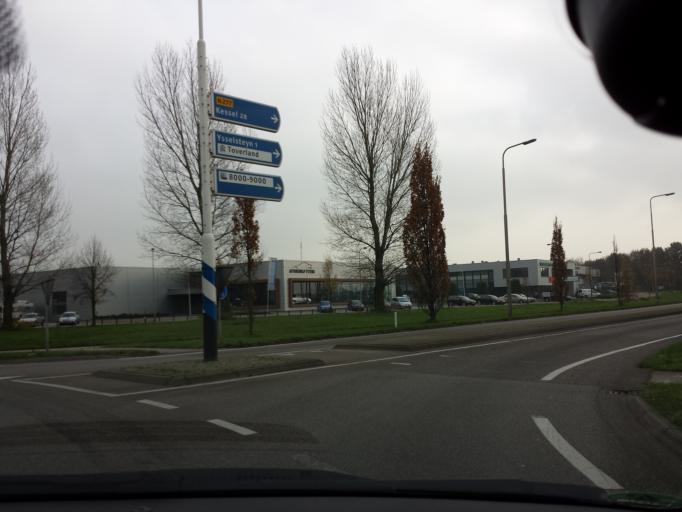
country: NL
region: Limburg
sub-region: Gemeente Venray
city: Venray
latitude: 51.4970
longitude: 5.8923
